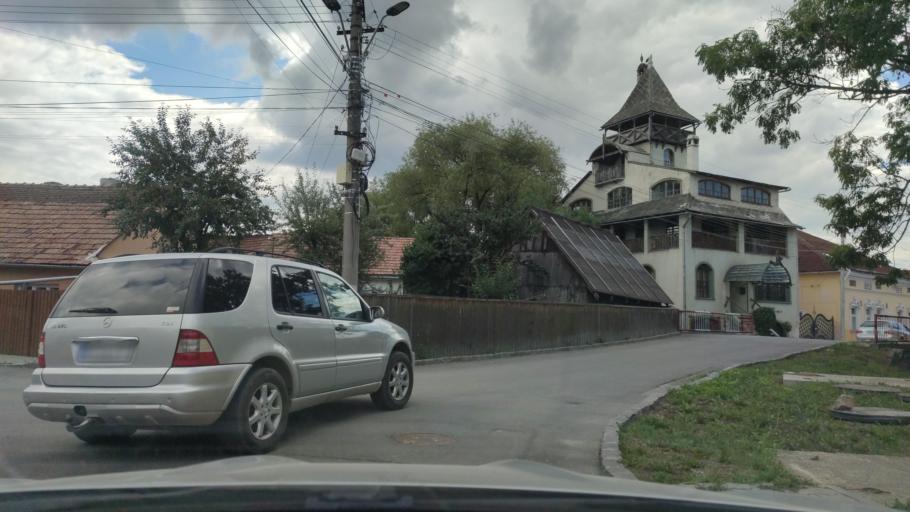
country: RO
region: Harghita
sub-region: Municipiul Gheorgheni
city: Gheorgheni
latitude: 46.7215
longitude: 25.6052
